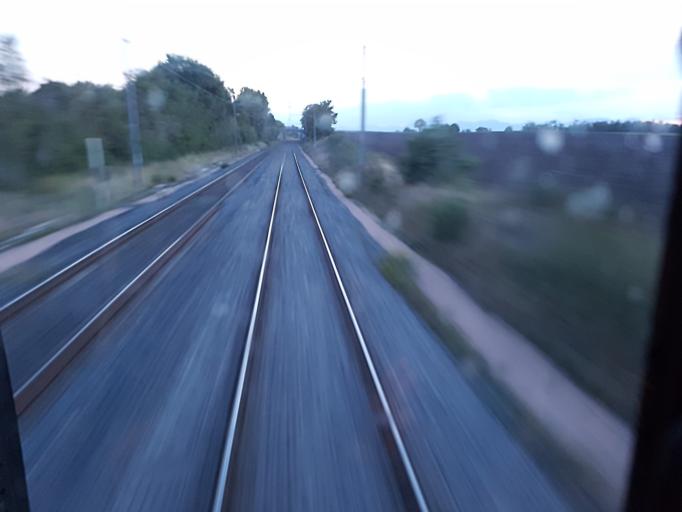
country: FR
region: Auvergne
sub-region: Departement du Puy-de-Dome
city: Ennezat
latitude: 45.9230
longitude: 3.2258
